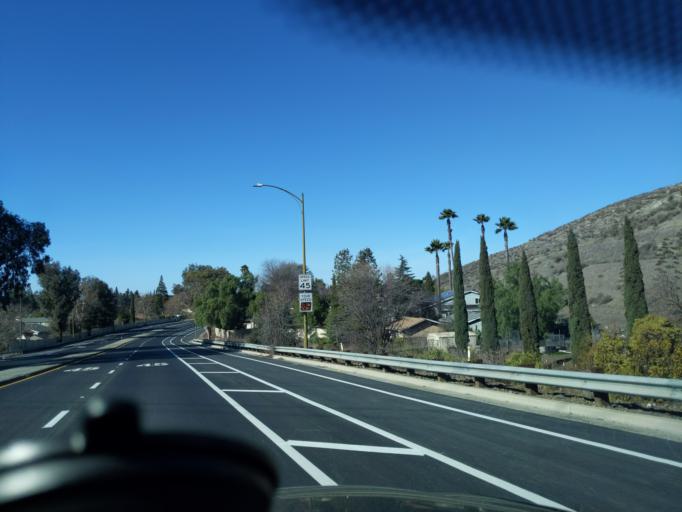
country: US
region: California
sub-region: Santa Clara County
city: Seven Trees
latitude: 37.2182
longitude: -121.7595
